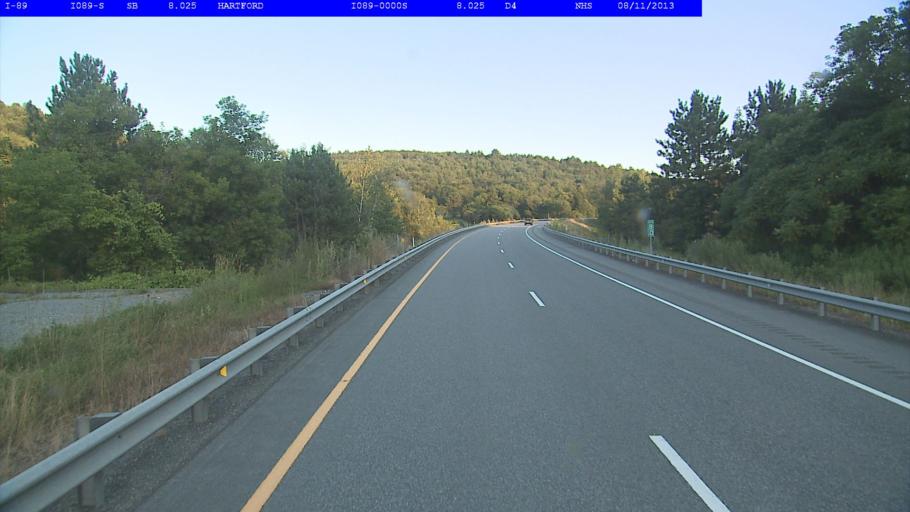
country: US
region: Vermont
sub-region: Windsor County
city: Wilder
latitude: 43.7202
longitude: -72.4147
